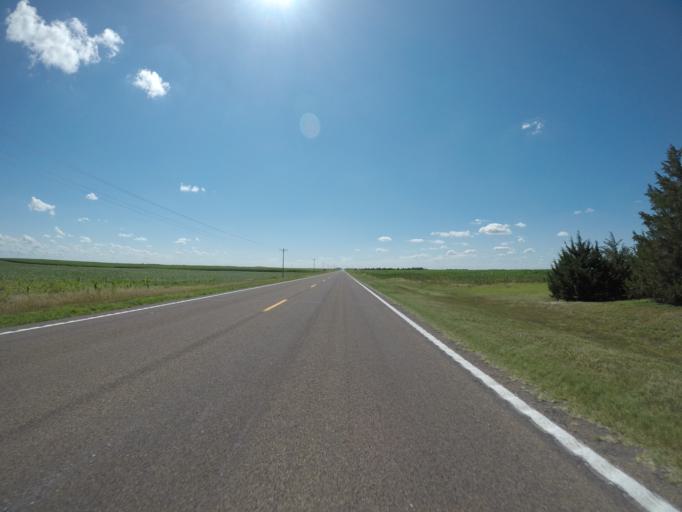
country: US
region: Nebraska
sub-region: Chase County
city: Imperial
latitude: 40.5377
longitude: -101.6778
